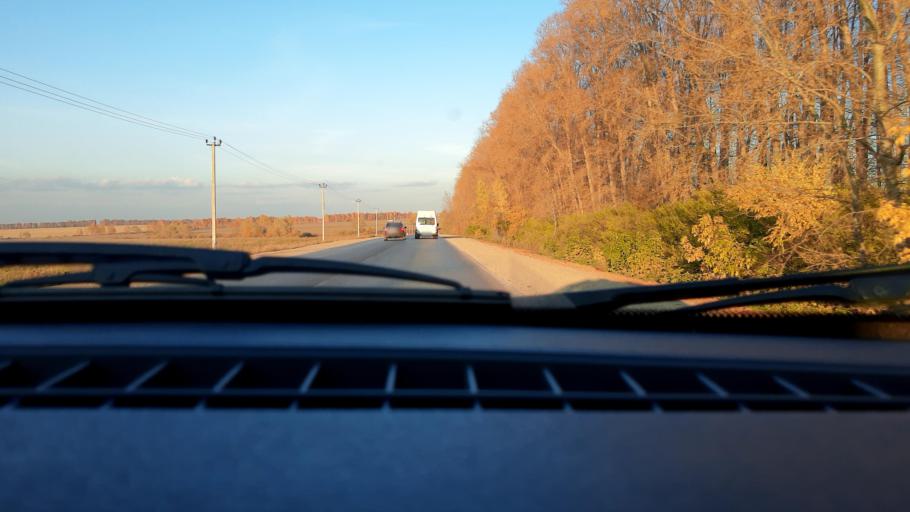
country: RU
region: Bashkortostan
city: Asanovo
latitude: 54.8210
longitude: 55.6129
